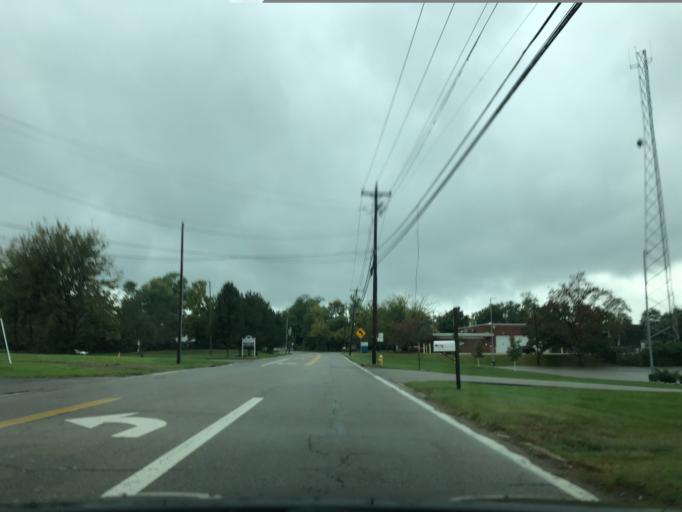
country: US
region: Ohio
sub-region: Hamilton County
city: Finneytown
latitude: 39.2076
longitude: -84.5056
